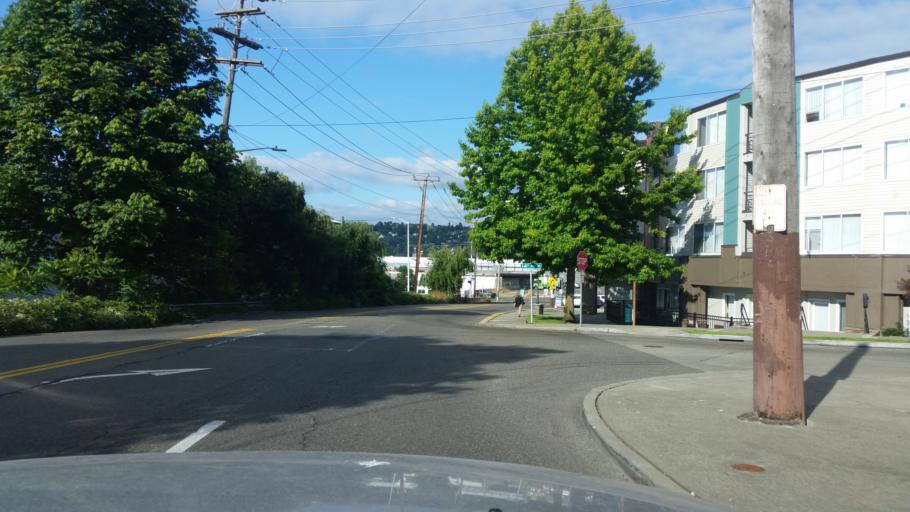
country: US
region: Washington
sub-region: King County
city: Seattle
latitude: 47.6550
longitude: -122.3752
